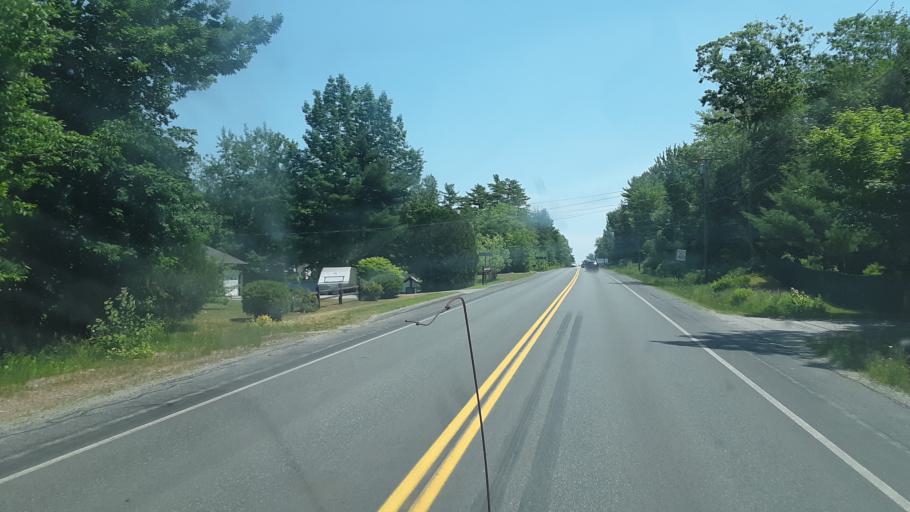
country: US
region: Maine
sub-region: Hancock County
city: Hancock
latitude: 44.5278
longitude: -68.2512
